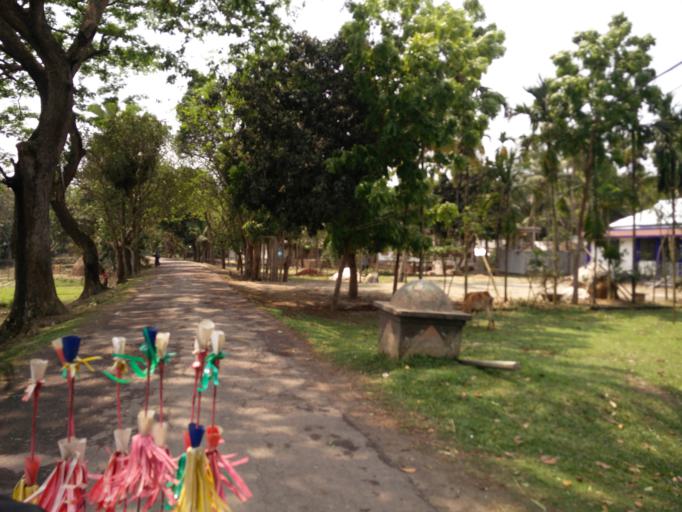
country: BD
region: Dhaka
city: Sherpur
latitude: 24.9502
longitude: 90.1625
